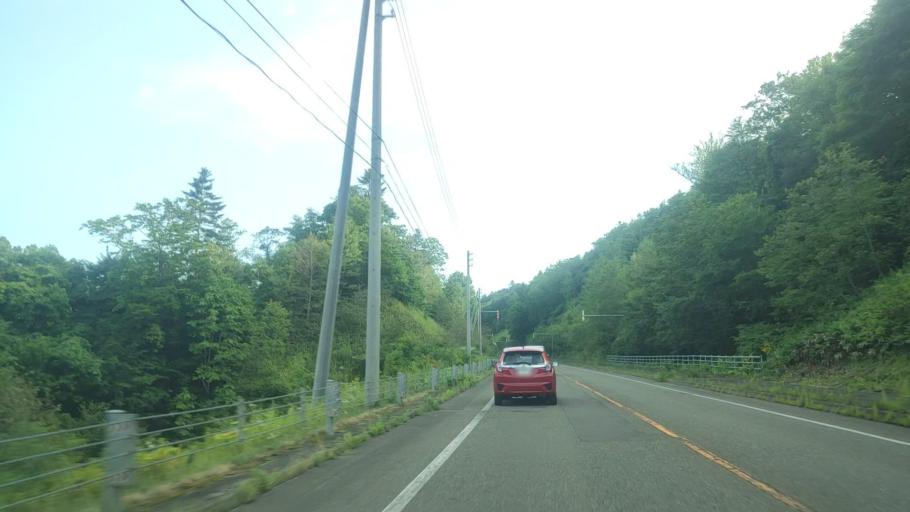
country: JP
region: Hokkaido
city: Iwamizawa
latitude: 43.0283
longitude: 141.9427
